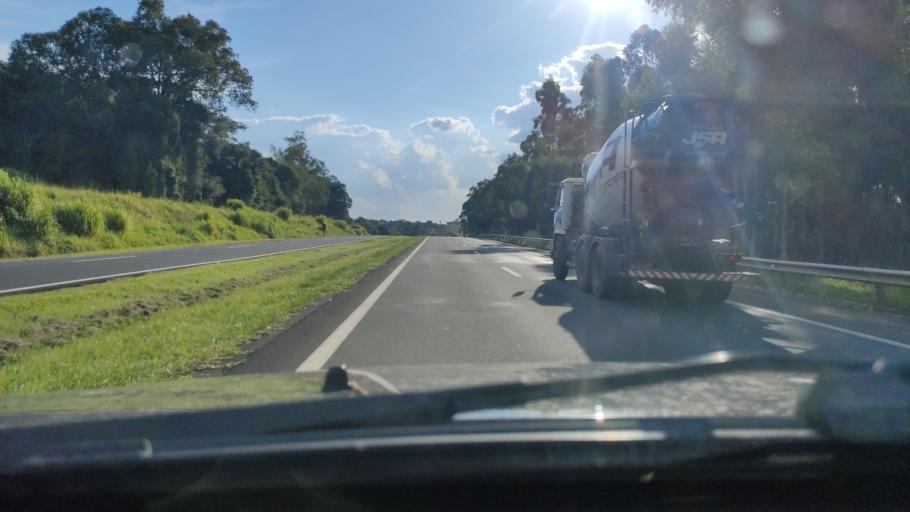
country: BR
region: Sao Paulo
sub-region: Itapira
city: Itapira
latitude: -22.4531
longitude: -46.8675
